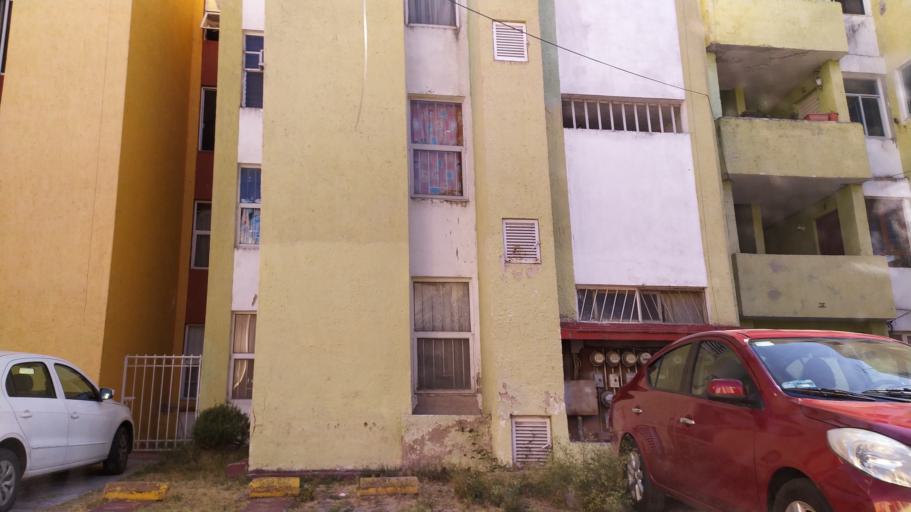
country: MX
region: Jalisco
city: Guadalajara
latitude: 20.6563
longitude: -103.4309
